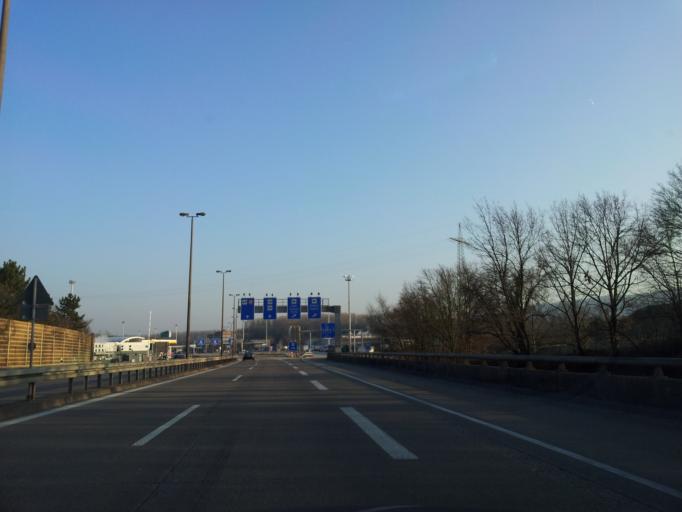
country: DE
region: Baden-Wuerttemberg
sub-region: Freiburg Region
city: Weil am Rhein
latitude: 47.5921
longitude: 7.6037
